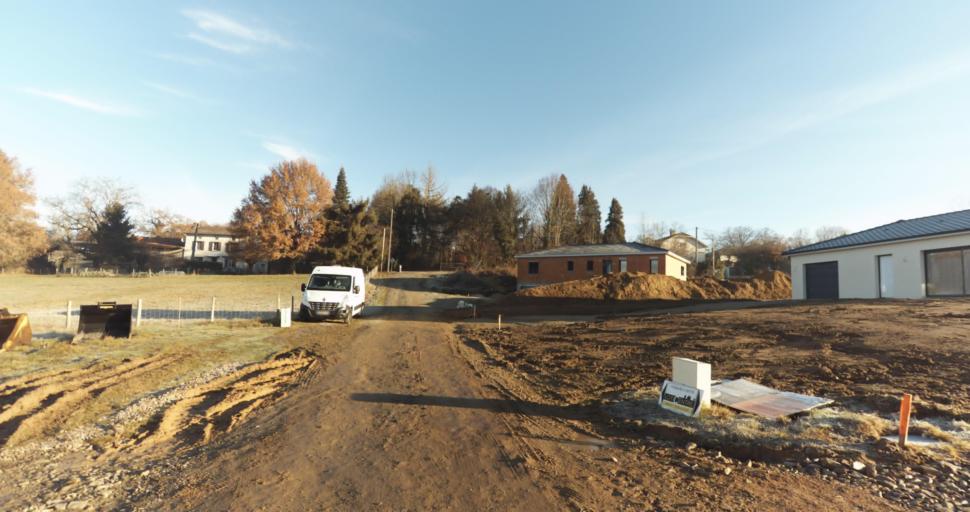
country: FR
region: Limousin
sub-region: Departement de la Haute-Vienne
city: Aixe-sur-Vienne
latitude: 45.8096
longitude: 1.1463
